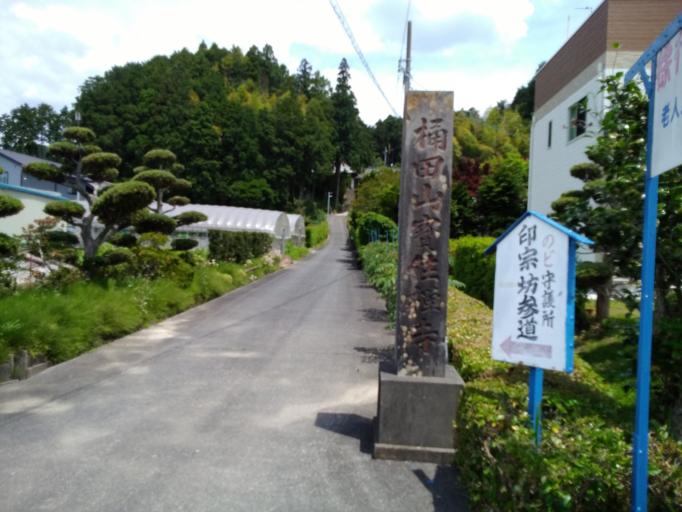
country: JP
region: Shizuoka
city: Kakegawa
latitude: 34.7467
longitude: 138.0558
